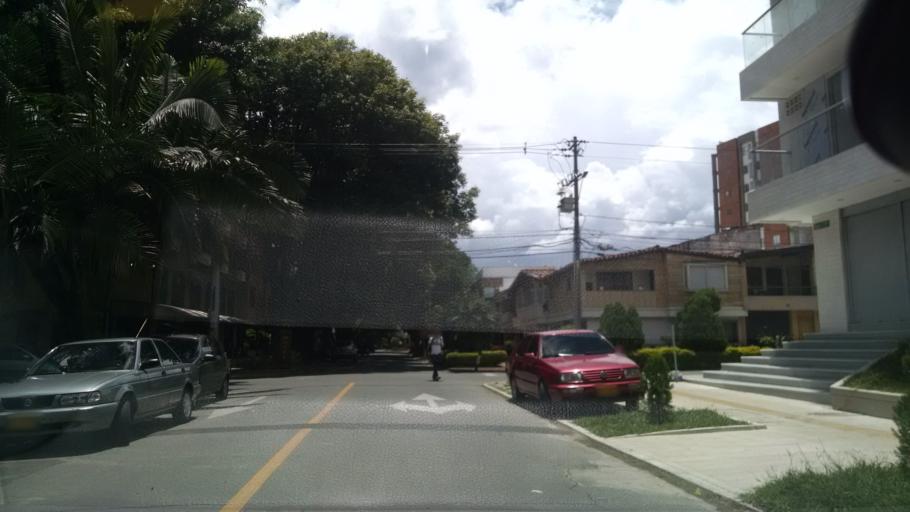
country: CO
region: Antioquia
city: Medellin
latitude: 6.2599
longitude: -75.5949
